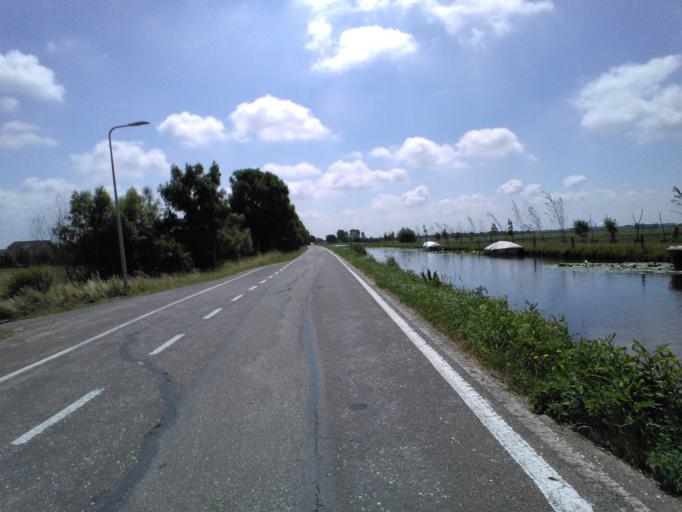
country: NL
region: South Holland
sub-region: Gemeente Maassluis
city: Maassluis
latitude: 51.9478
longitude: 4.2946
